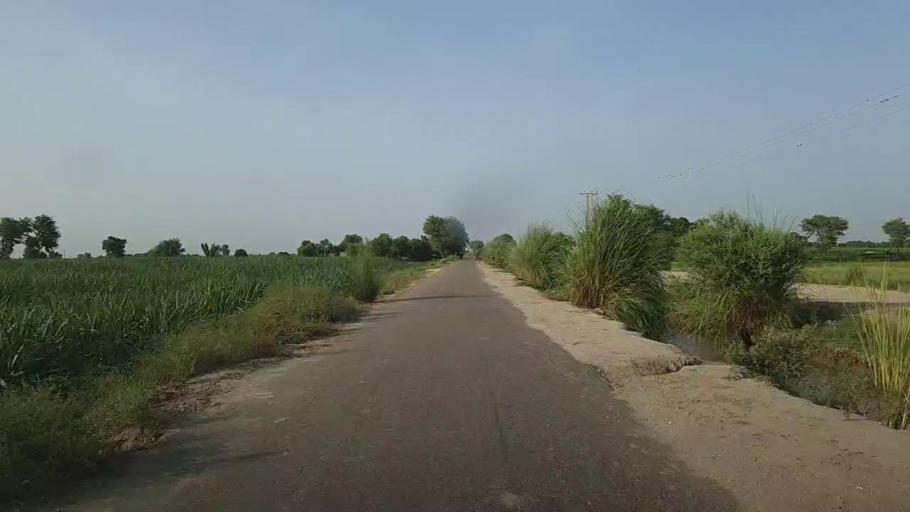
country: PK
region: Sindh
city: Ubauro
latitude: 28.0948
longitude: 69.8213
